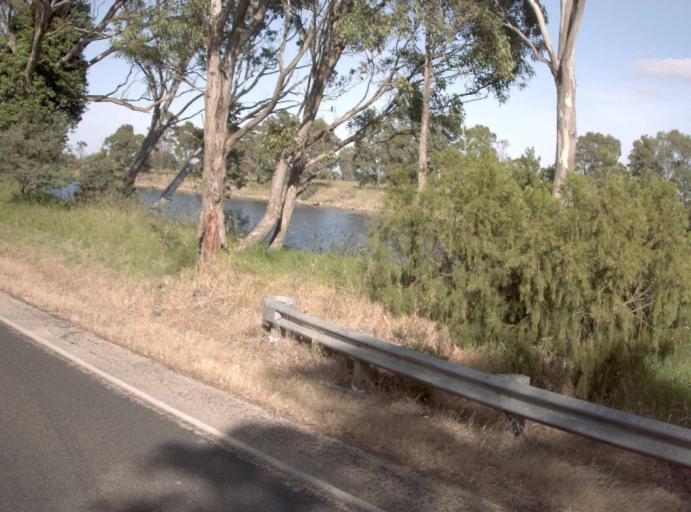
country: AU
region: Victoria
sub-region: East Gippsland
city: Lakes Entrance
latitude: -37.8423
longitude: 147.8564
